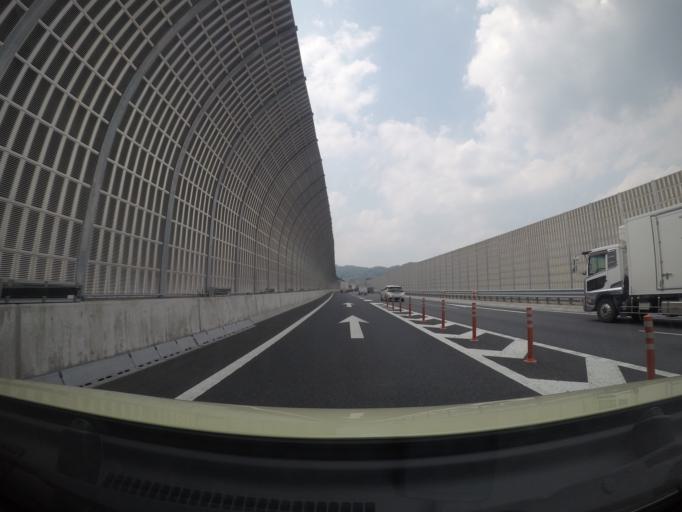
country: JP
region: Tokyo
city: Hachioji
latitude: 35.5833
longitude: 139.2917
